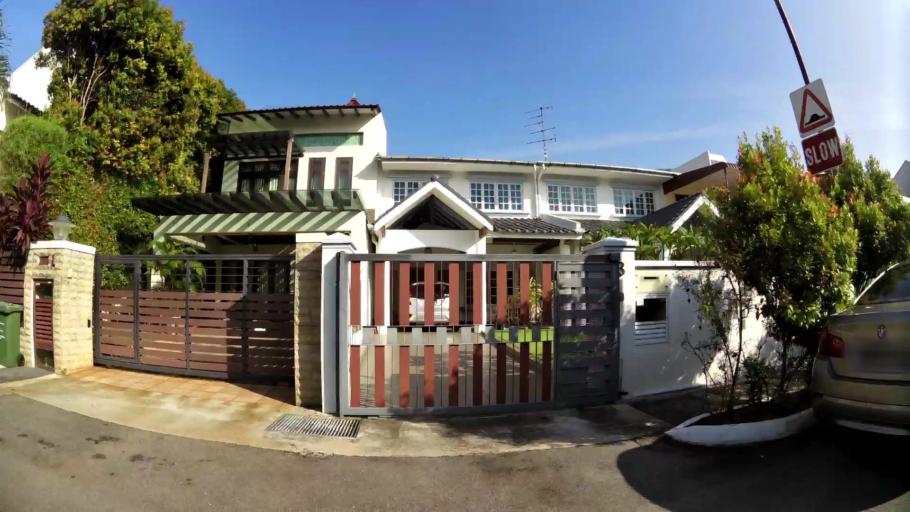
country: SG
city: Singapore
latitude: 1.3148
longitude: 103.9232
